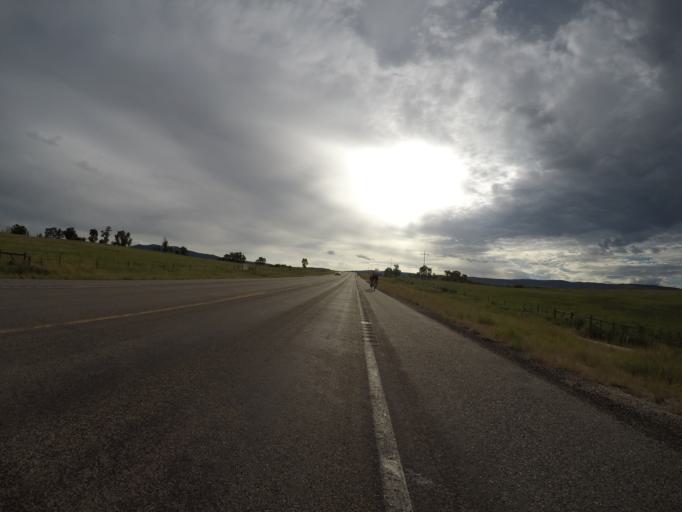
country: US
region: Wyoming
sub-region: Carbon County
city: Saratoga
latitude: 41.3510
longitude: -106.6225
